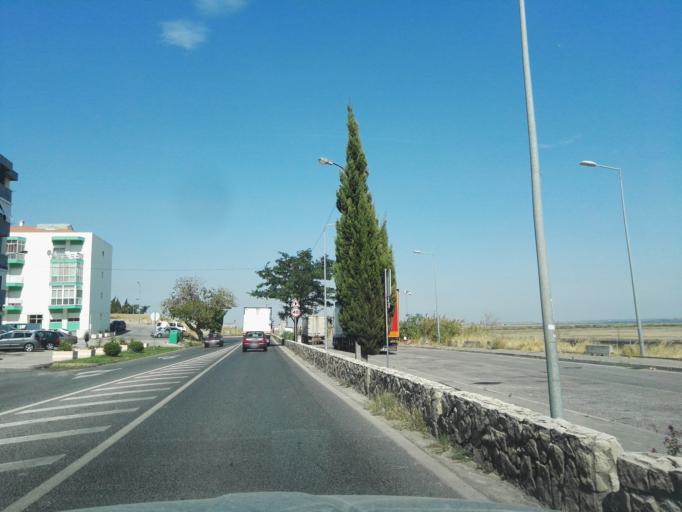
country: PT
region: Lisbon
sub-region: Vila Franca de Xira
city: Vialonga
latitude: 38.8738
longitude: -9.0538
